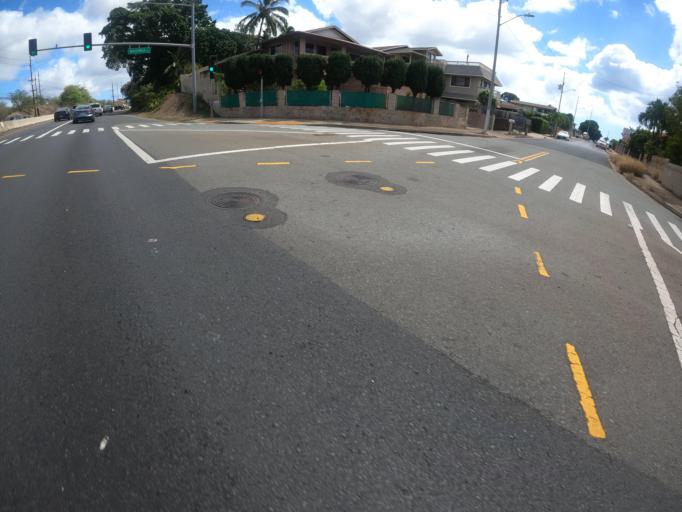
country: US
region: Hawaii
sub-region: Honolulu County
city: Makakilo City
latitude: 21.3439
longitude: -158.1132
